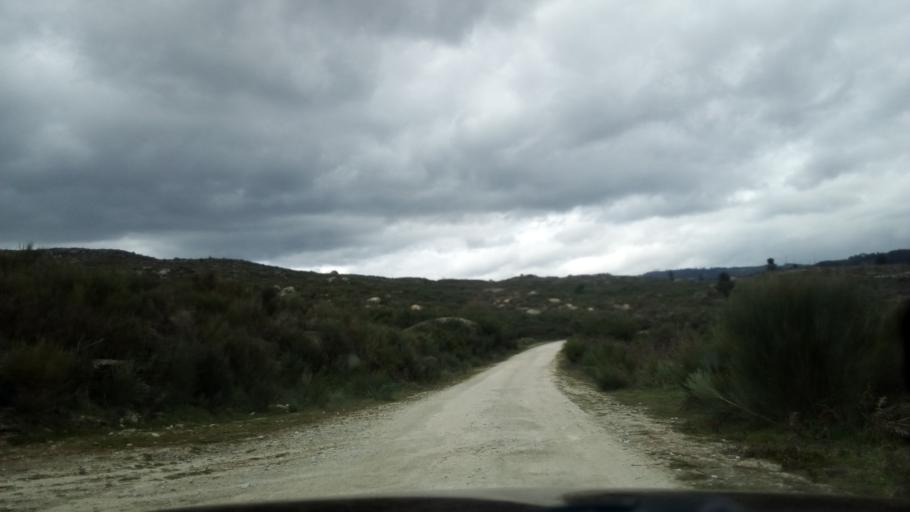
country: PT
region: Guarda
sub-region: Fornos de Algodres
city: Fornos de Algodres
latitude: 40.5938
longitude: -7.5705
